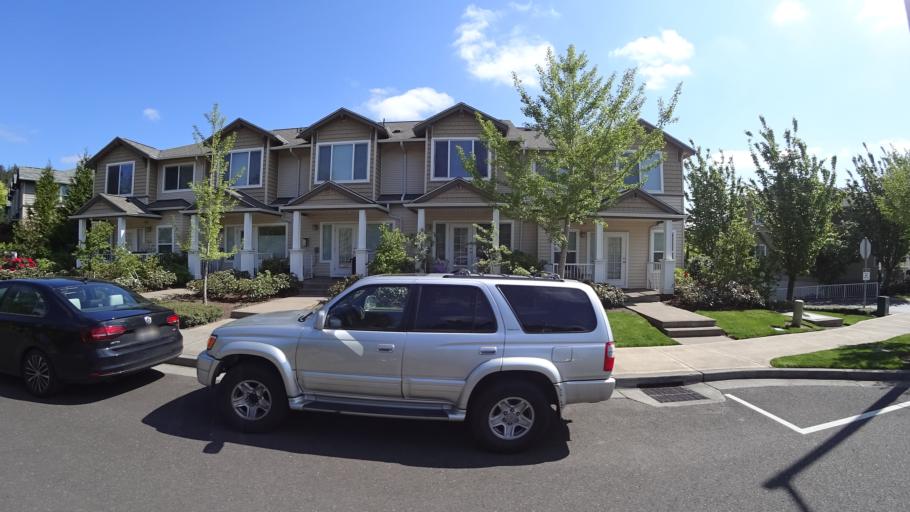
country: US
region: Oregon
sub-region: Washington County
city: King City
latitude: 45.4285
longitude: -122.8359
